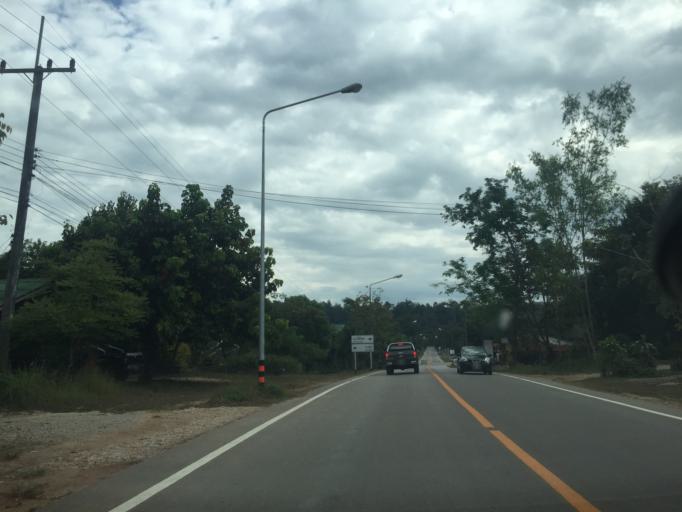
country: TH
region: Lampang
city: Mueang Pan
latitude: 18.8215
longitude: 99.5048
